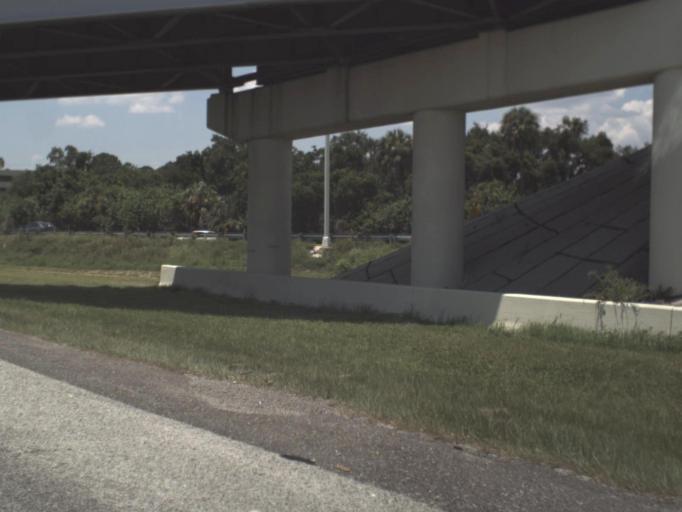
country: US
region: Florida
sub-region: Hillsborough County
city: Tampa
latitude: 27.9473
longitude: -82.5328
